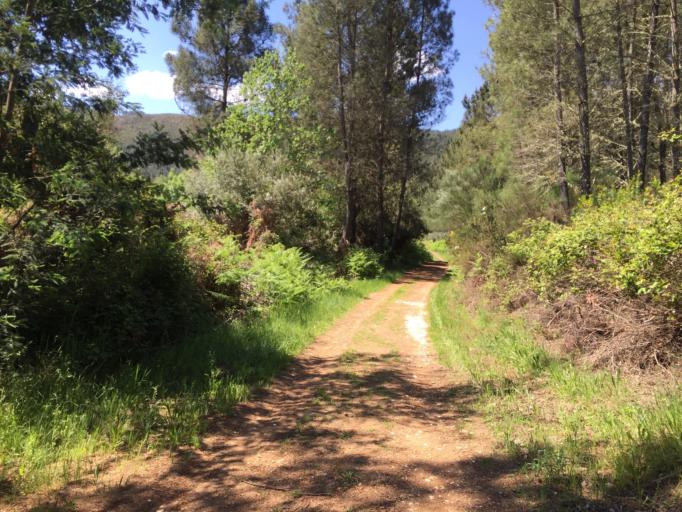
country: PT
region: Coimbra
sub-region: Pampilhosa da Serra
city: Pampilhosa da Serra
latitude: 40.0718
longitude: -7.7755
